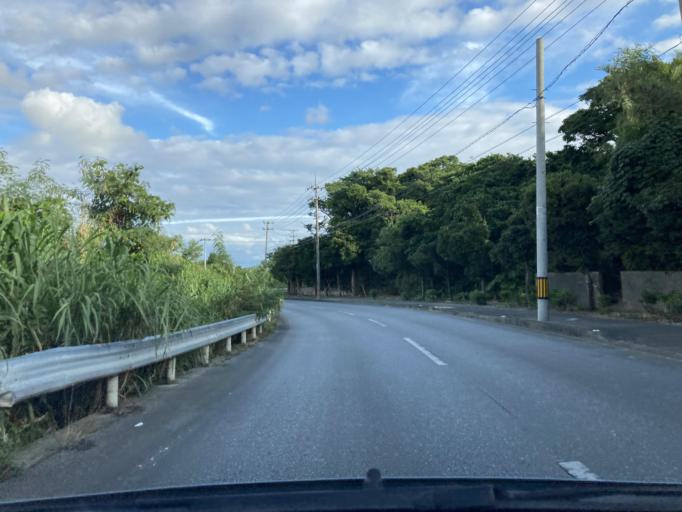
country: JP
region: Okinawa
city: Itoman
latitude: 26.1340
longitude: 127.7508
